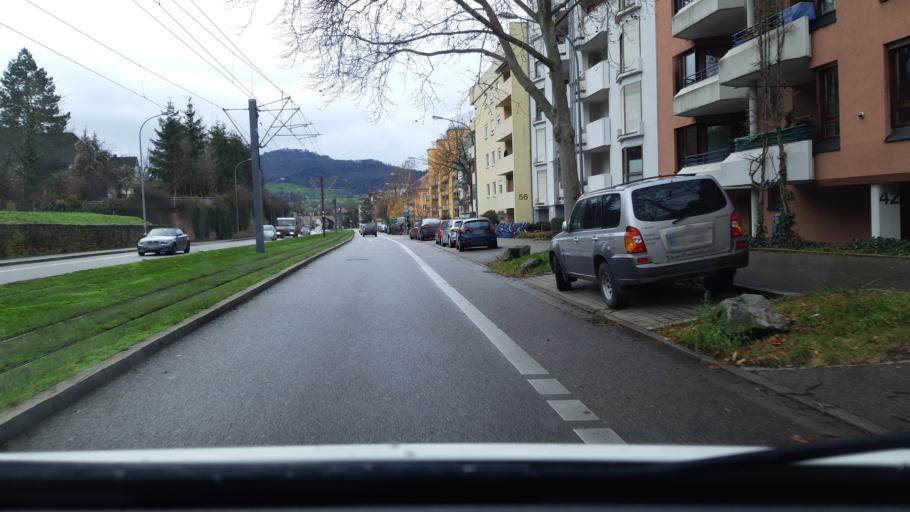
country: DE
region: Baden-Wuerttemberg
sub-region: Freiburg Region
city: Merzhausen
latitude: 47.9834
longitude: 7.8360
